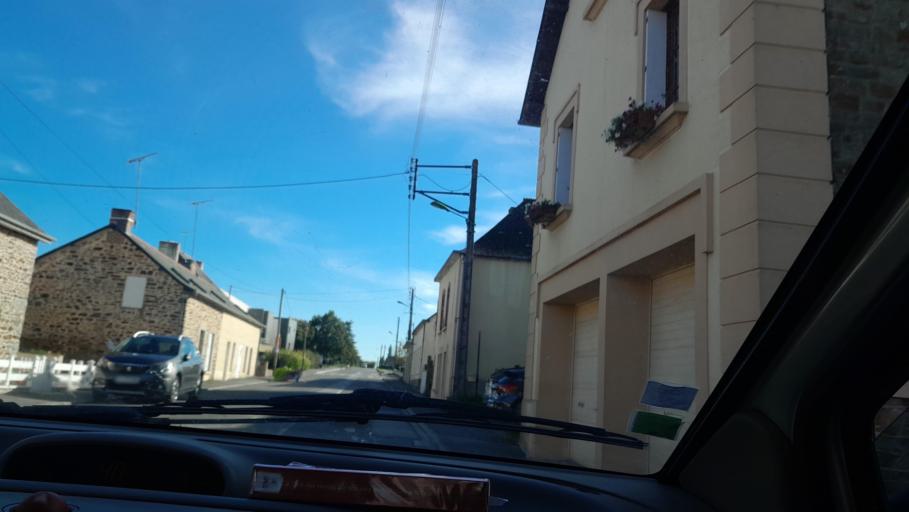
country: FR
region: Brittany
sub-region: Departement d'Ille-et-Vilaine
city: Argentre-du-Plessis
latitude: 48.0526
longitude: -1.1498
